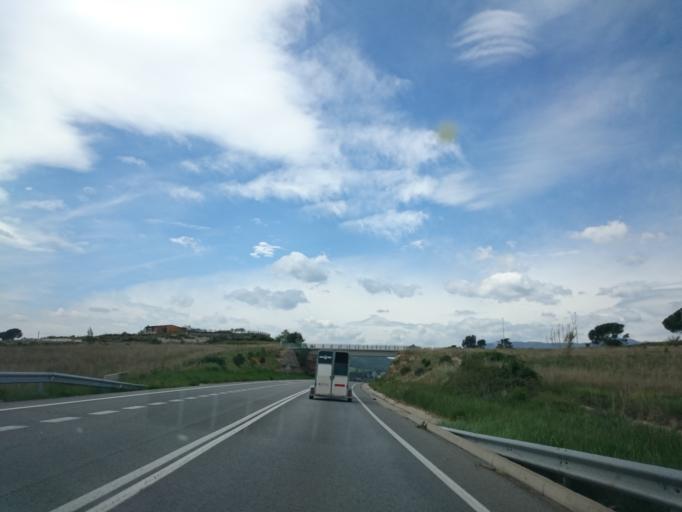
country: ES
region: Catalonia
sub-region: Provincia de Barcelona
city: Gironella
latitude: 42.0478
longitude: 1.8881
